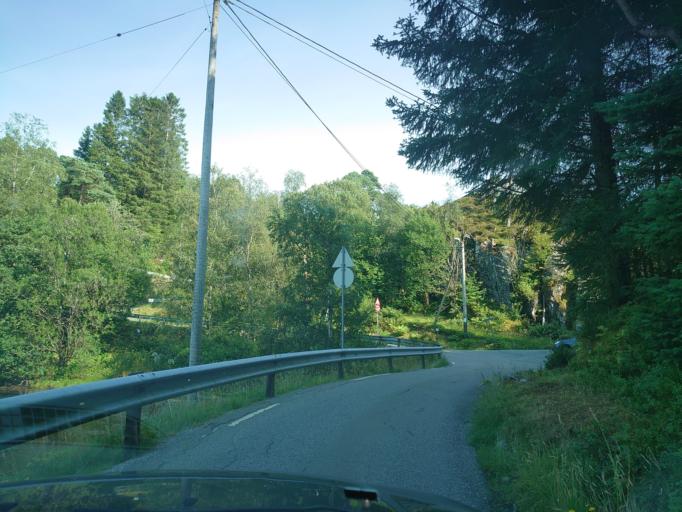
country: NO
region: Hordaland
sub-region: Bergen
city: Sandsli
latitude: 60.2702
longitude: 5.2686
